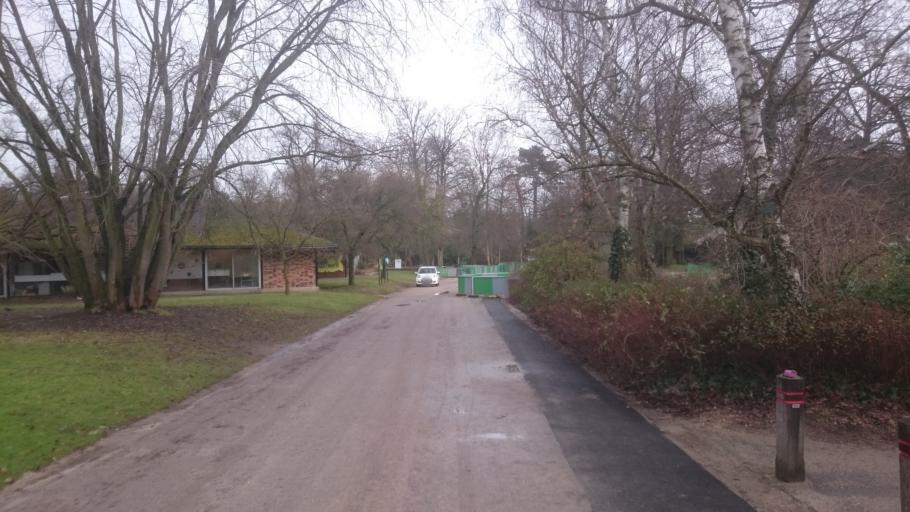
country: FR
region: Ile-de-France
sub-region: Departement du Val-de-Marne
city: Vincennes
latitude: 48.8394
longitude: 2.4421
